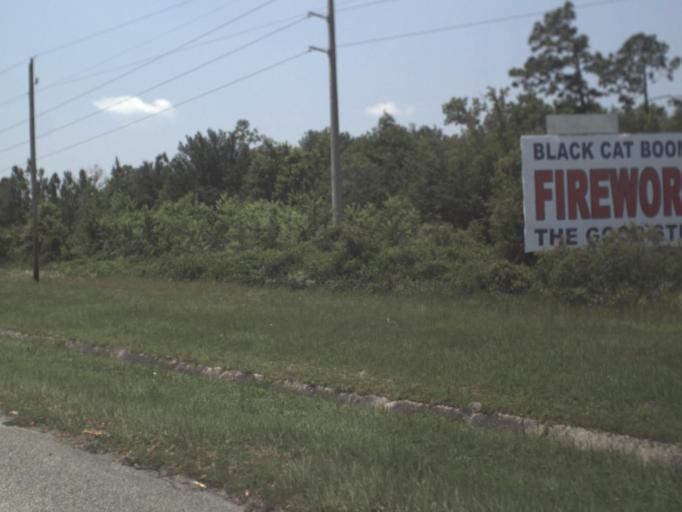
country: US
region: Florida
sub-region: Baker County
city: Macclenny
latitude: 30.1423
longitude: -82.0366
